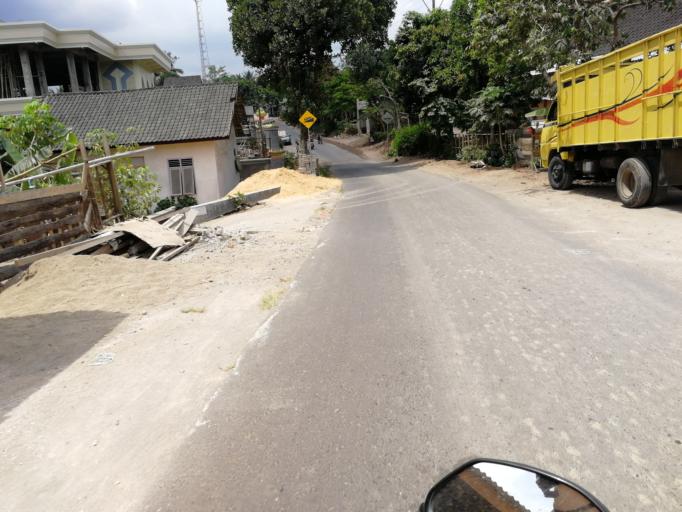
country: ID
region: West Nusa Tenggara
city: Pediti
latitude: -8.5678
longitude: 116.3303
